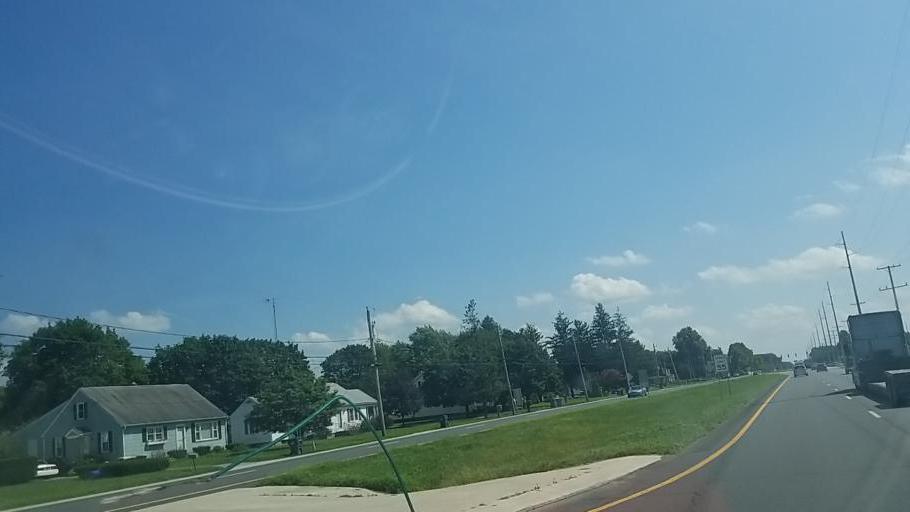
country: US
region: Delaware
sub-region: Sussex County
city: Milford
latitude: 38.8997
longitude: -75.4398
